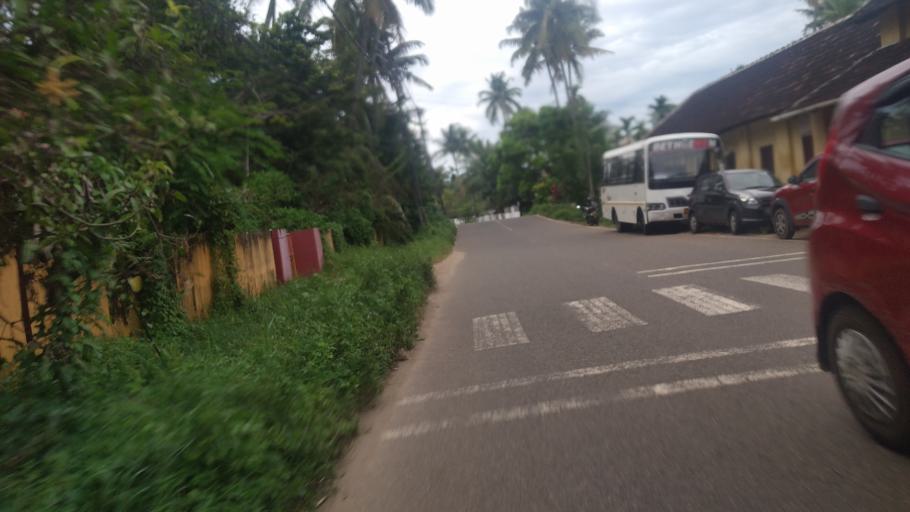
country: IN
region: Kerala
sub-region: Ernakulam
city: Cochin
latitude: 9.8942
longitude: 76.2589
